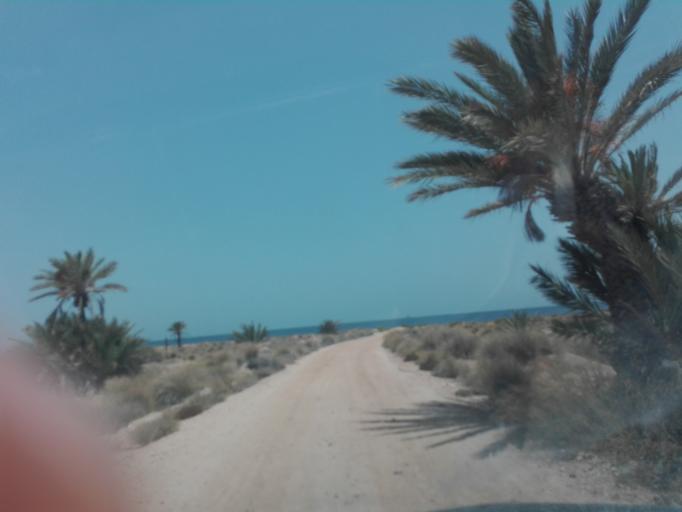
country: TN
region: Safaqis
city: Al Qarmadah
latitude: 34.6677
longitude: 11.0933
